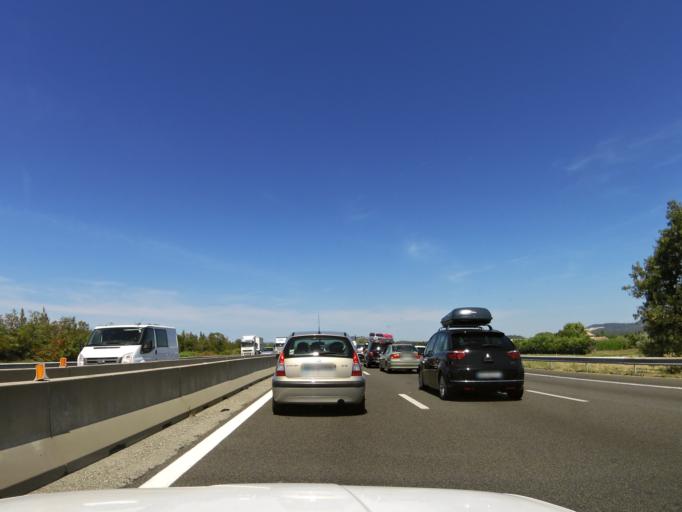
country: FR
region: Rhone-Alpes
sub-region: Departement de la Drome
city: La Garde-Adhemar
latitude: 44.3924
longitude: 4.7302
